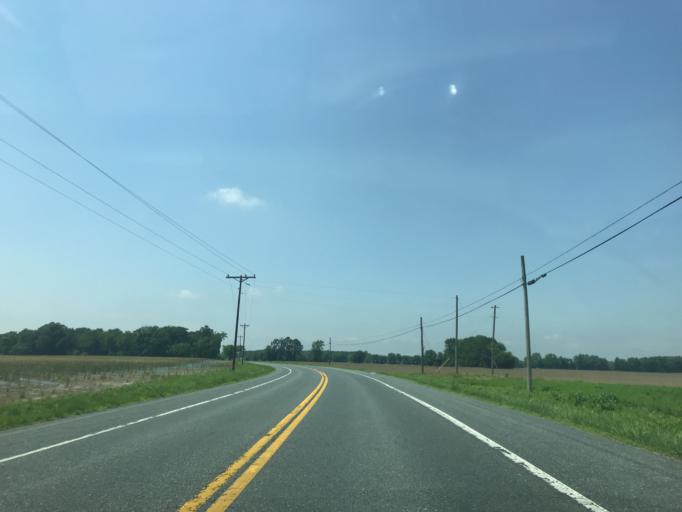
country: US
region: Maryland
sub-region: Caroline County
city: Federalsburg
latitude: 38.6446
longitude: -75.7134
